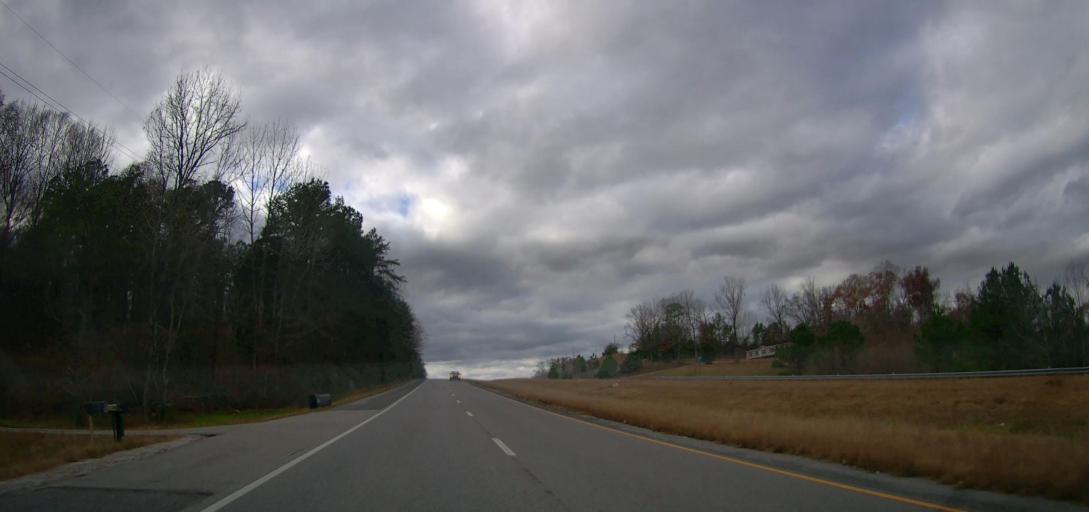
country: US
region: Alabama
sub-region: Lawrence County
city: Moulton
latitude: 34.5572
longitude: -87.3336
